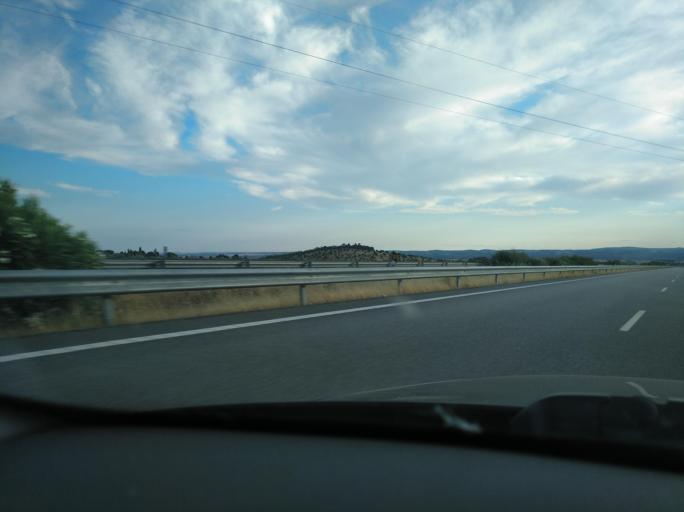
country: PT
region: Portalegre
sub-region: Elvas
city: Elvas
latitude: 38.8746
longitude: -7.2757
